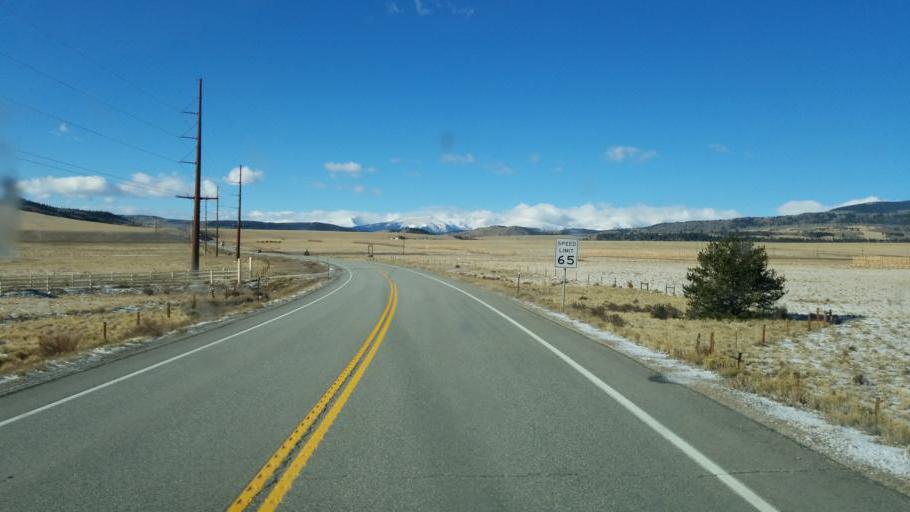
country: US
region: Colorado
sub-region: Park County
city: Fairplay
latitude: 39.2976
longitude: -105.9001
